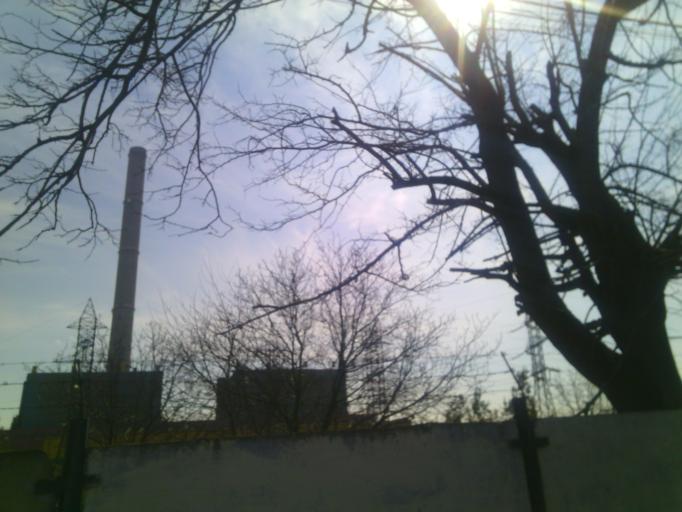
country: RO
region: Ilfov
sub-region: Comuna Jilava
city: Jilava
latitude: 44.3728
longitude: 26.1031
